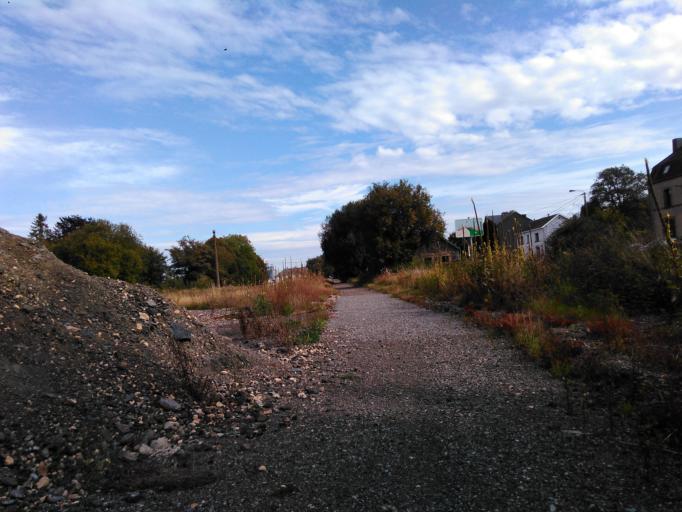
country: BE
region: Wallonia
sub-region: Province du Luxembourg
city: Vaux-sur-Sure
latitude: 49.9170
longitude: 5.5040
